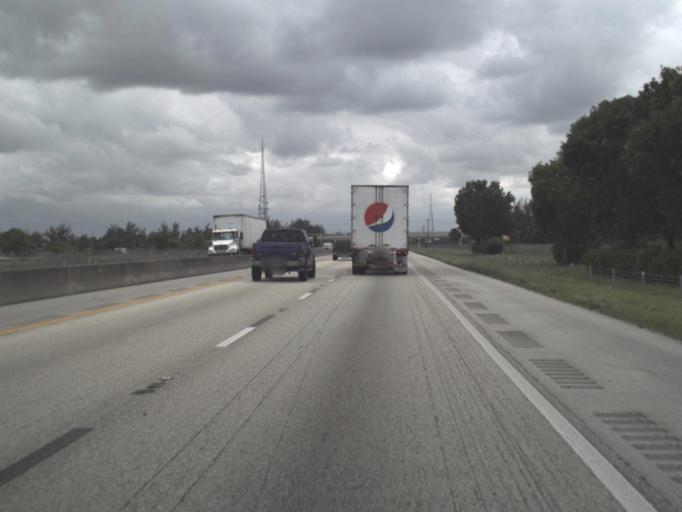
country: US
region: Florida
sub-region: Palm Beach County
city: Lake Belvedere Estates
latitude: 26.6563
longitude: -80.1743
